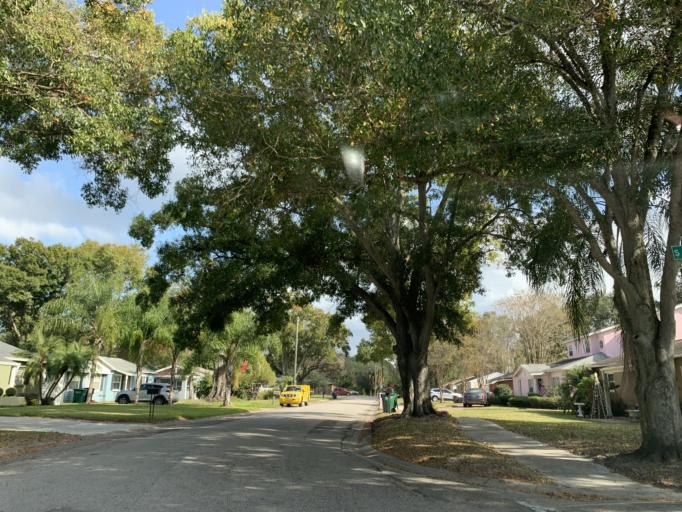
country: US
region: Florida
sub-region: Hillsborough County
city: Tampa
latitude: 27.9079
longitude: -82.5136
